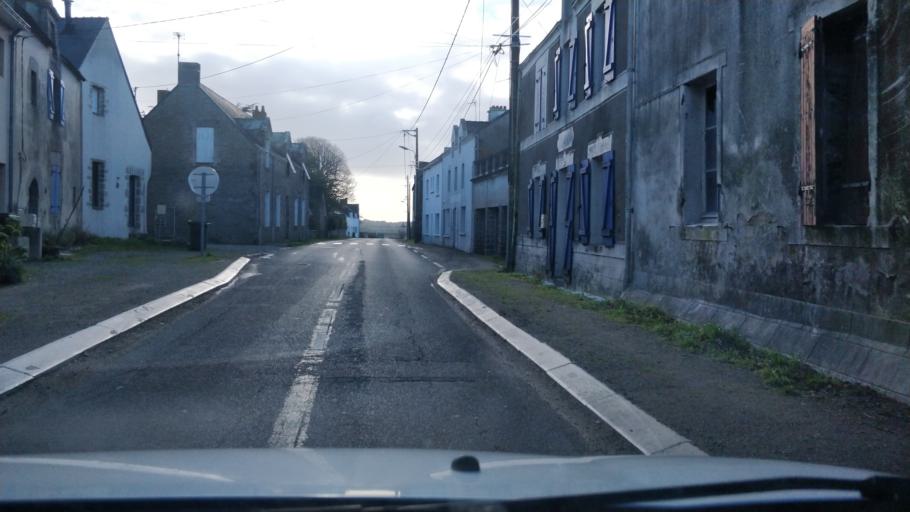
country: FR
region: Pays de la Loire
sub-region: Departement de la Loire-Atlantique
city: Asserac
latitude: 47.4146
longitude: -2.3998
